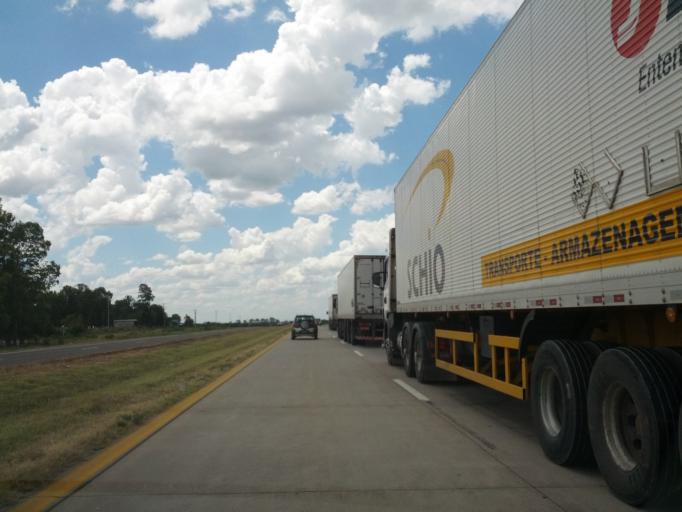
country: AR
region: Entre Rios
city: Gualeguaychu
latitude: -32.9976
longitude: -58.6005
